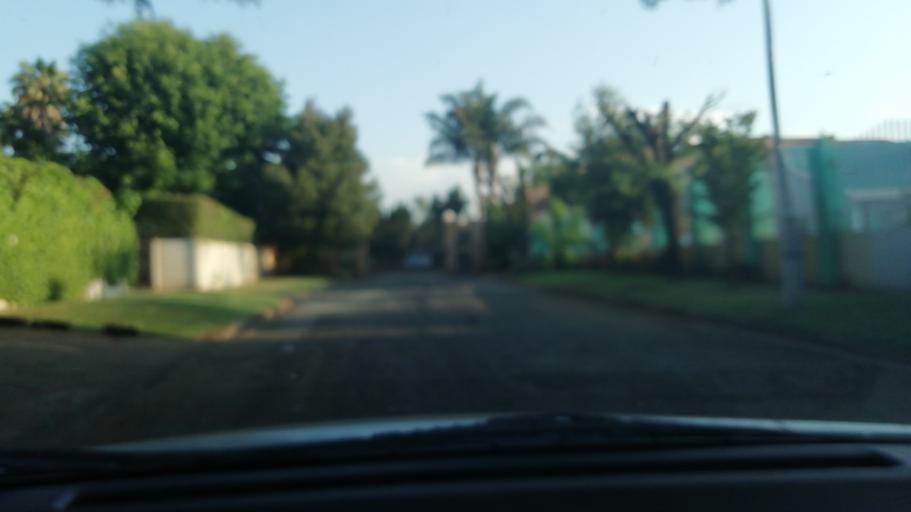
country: ZA
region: Gauteng
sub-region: Ekurhuleni Metropolitan Municipality
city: Boksburg
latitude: -26.1933
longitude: 28.2835
